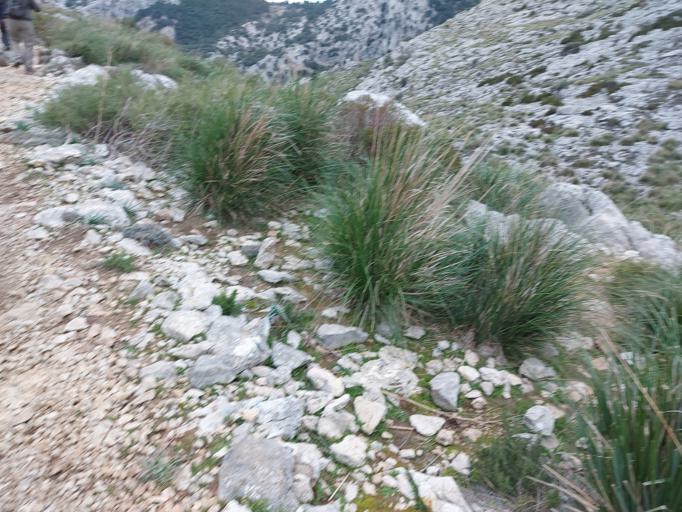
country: ES
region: Balearic Islands
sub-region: Illes Balears
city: Fornalutx
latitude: 39.7828
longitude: 2.8028
